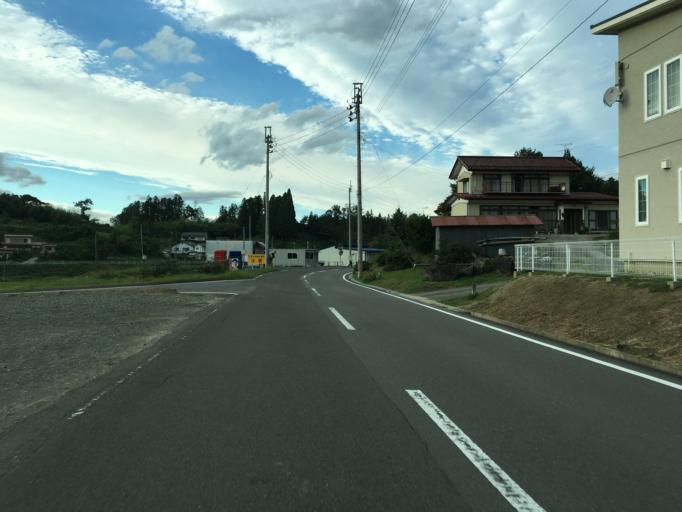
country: JP
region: Fukushima
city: Nihommatsu
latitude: 37.6151
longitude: 140.4951
